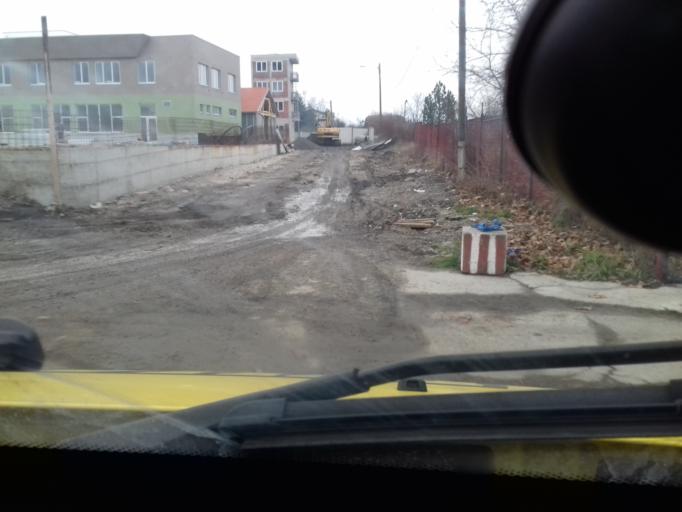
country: BA
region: Federation of Bosnia and Herzegovina
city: Zenica
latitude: 44.1923
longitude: 17.9301
